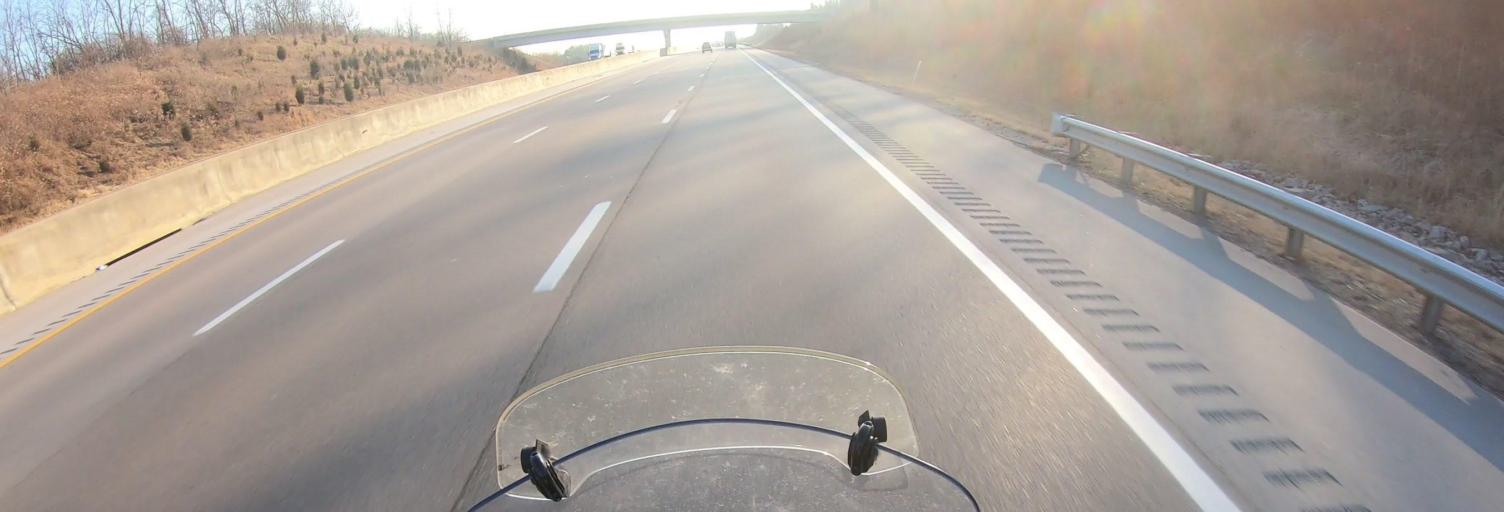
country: US
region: Kentucky
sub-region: Grant County
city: Williamstown
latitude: 38.5992
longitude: -84.5825
